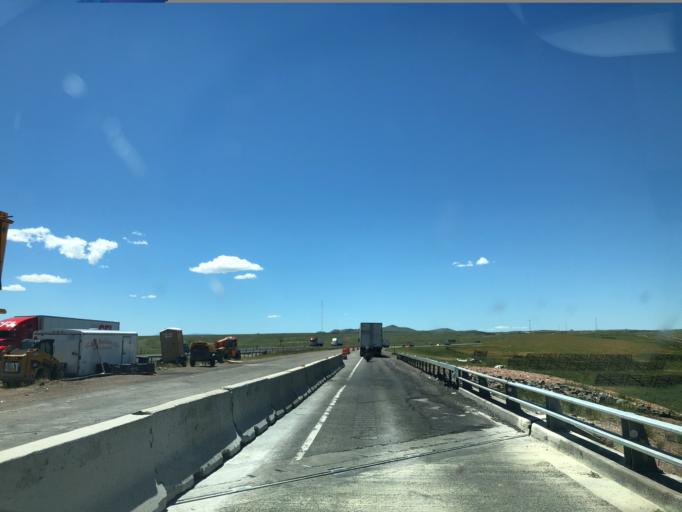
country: US
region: Wyoming
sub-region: Laramie County
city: Cheyenne
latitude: 41.0984
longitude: -105.0994
